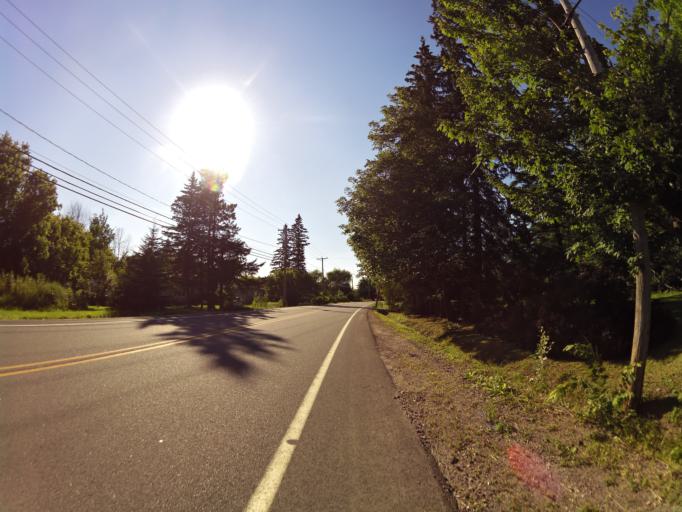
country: CA
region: Quebec
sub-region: Outaouais
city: Gatineau
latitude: 45.4912
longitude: -75.7663
